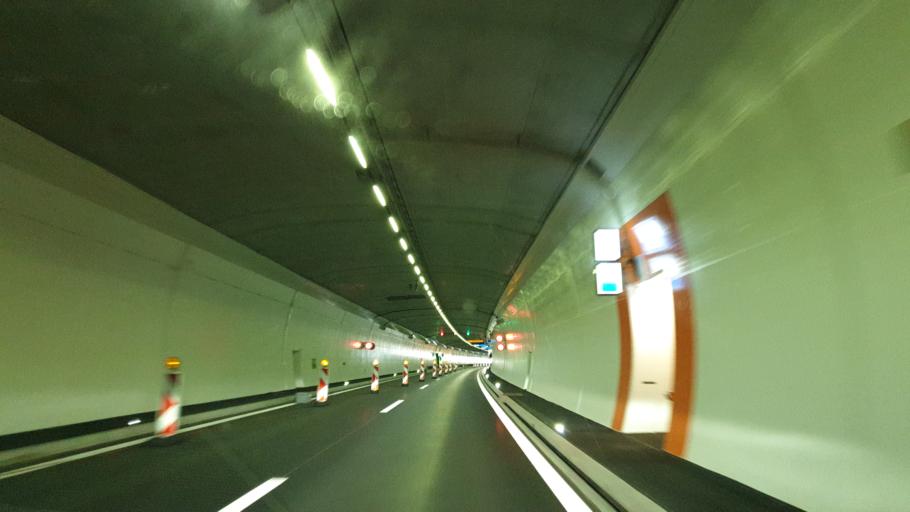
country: CH
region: Valais
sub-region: Visp District
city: Visp
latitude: 46.2819
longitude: 7.8933
